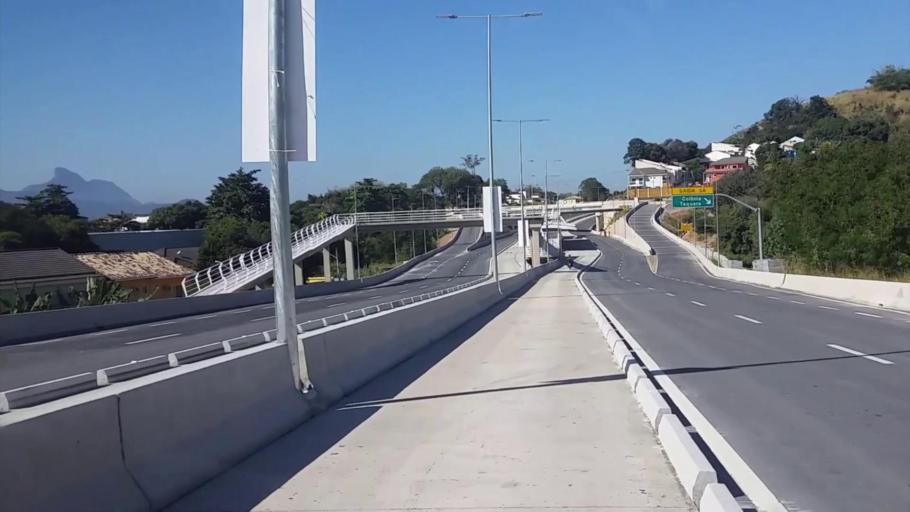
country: BR
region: Rio de Janeiro
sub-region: Nilopolis
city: Nilopolis
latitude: -22.9170
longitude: -43.3971
